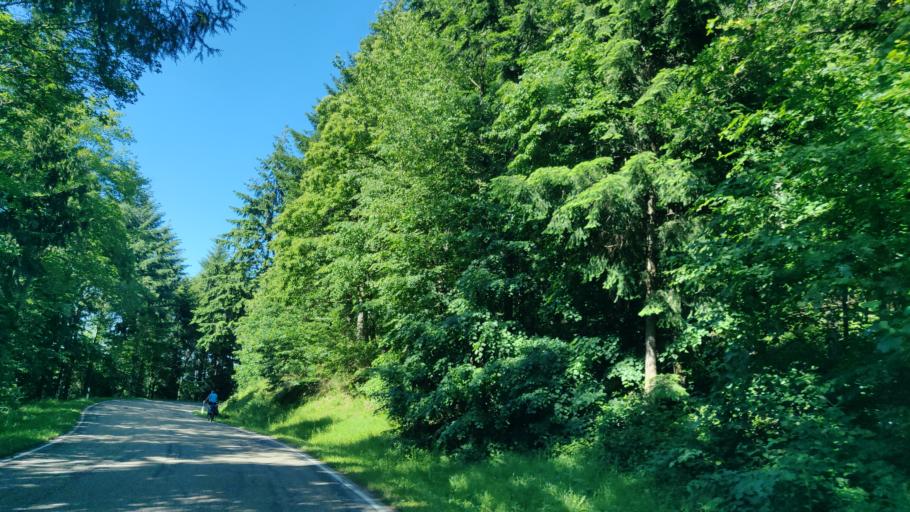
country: DE
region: Baden-Wuerttemberg
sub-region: Karlsruhe Region
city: Gernsbach
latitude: 48.7487
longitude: 8.3127
